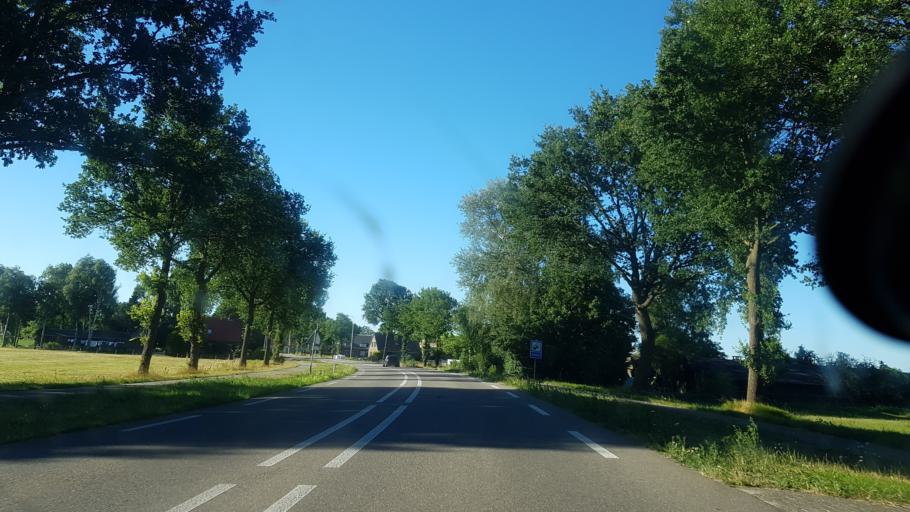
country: NL
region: Gelderland
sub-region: Gemeente Brummen
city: Eerbeek
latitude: 52.1610
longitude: 6.0558
